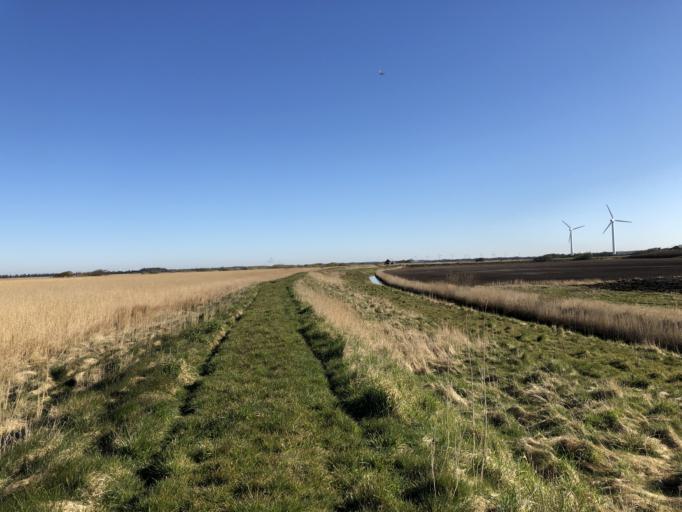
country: DK
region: Central Jutland
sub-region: Holstebro Kommune
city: Ulfborg
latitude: 56.3068
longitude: 8.2923
